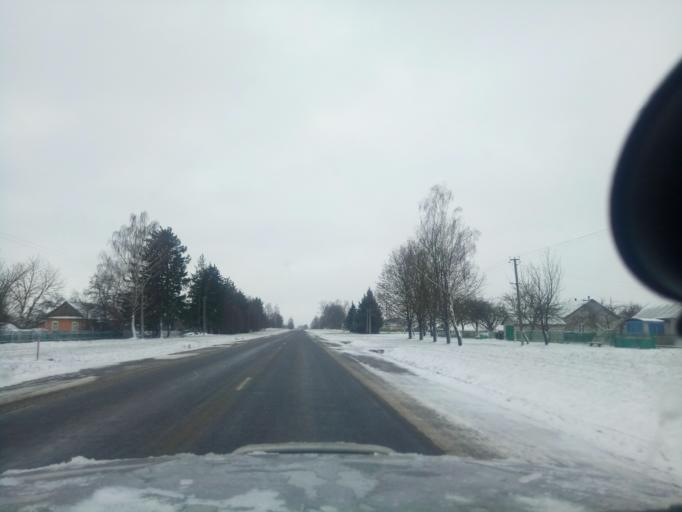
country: BY
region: Minsk
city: Klyetsk
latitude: 53.1219
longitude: 26.6664
